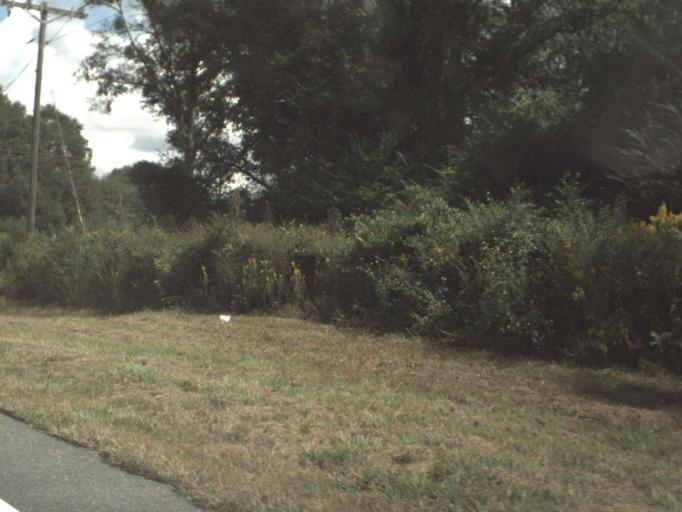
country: US
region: Florida
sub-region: Washington County
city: Chipley
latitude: 30.7999
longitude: -85.5180
